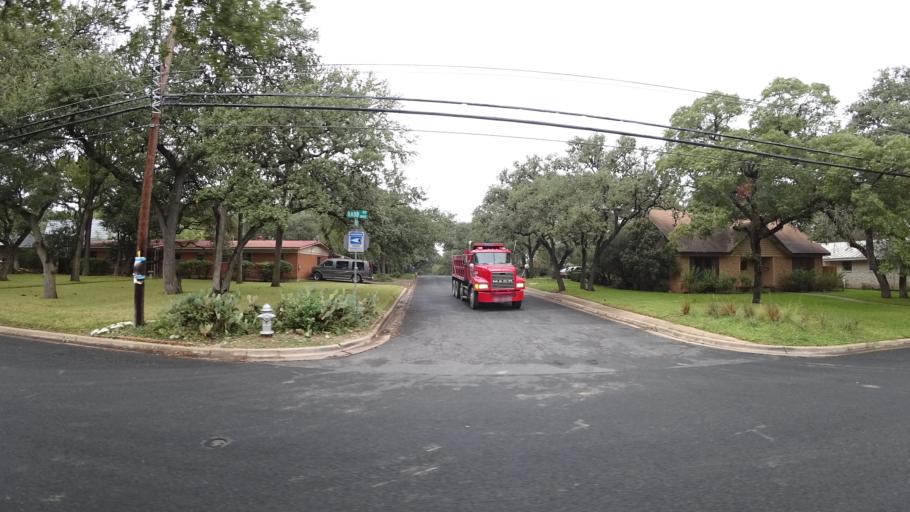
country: US
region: Texas
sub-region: Travis County
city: Rollingwood
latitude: 30.2555
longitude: -97.7764
